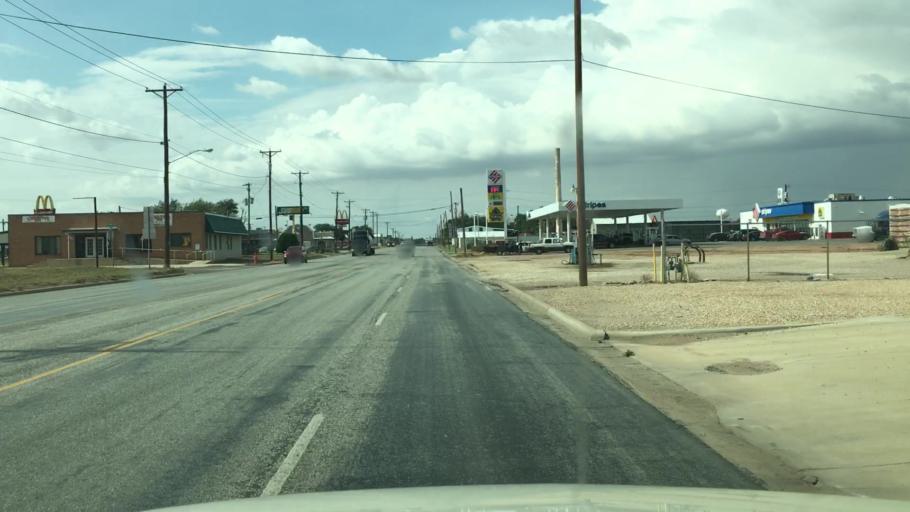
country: US
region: Texas
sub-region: Dawson County
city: Lamesa
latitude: 32.7353
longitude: -101.9497
